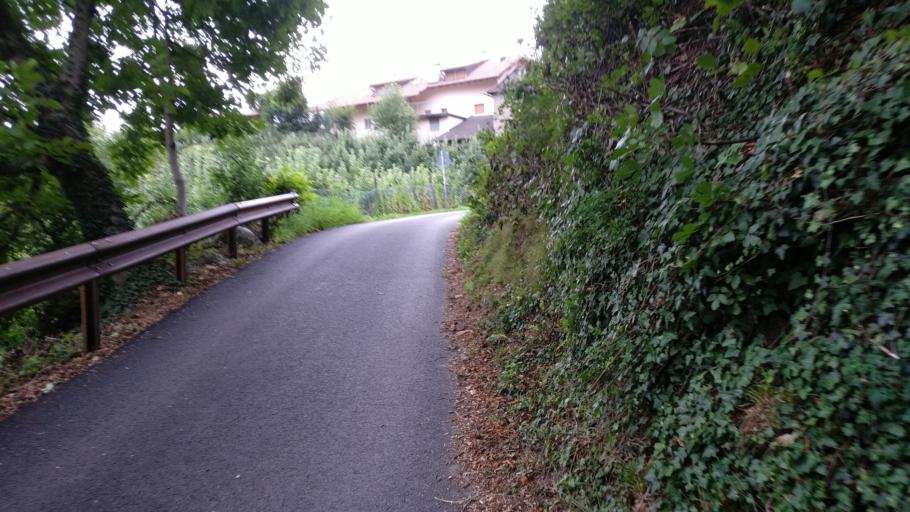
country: IT
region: Trentino-Alto Adige
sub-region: Bolzano
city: San Paolo
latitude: 46.4884
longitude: 11.2469
